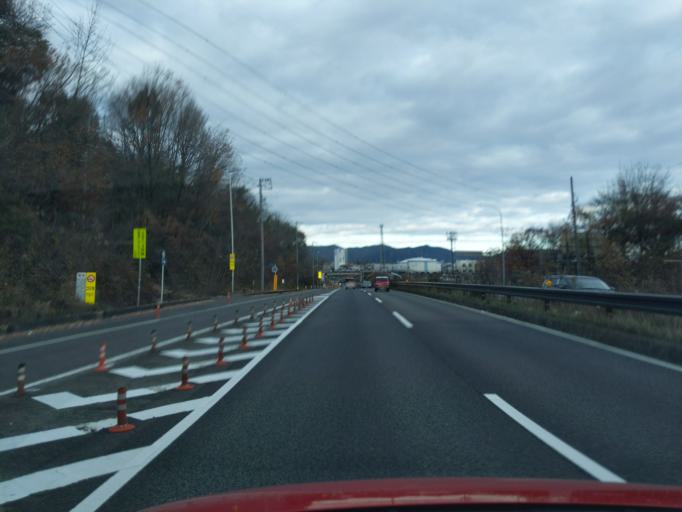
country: JP
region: Aichi
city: Kasugai
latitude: 35.2783
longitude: 137.0118
